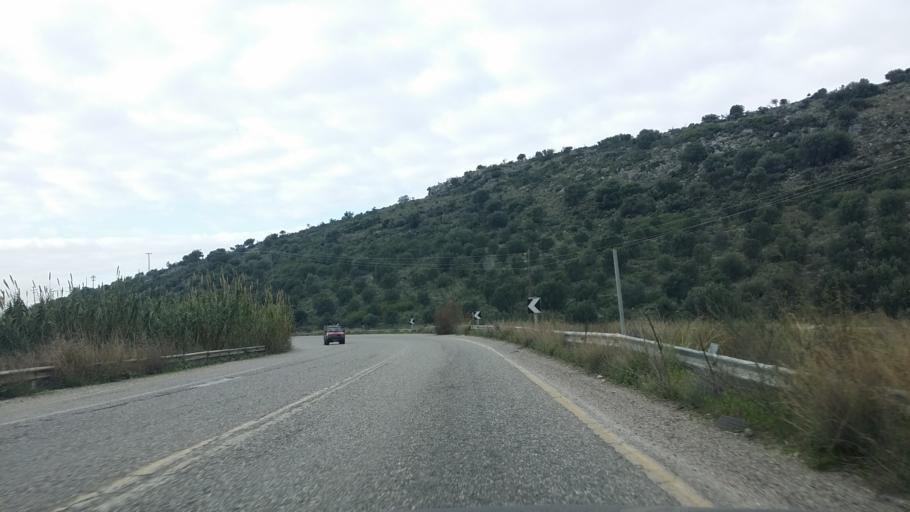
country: GR
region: West Greece
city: Aitoliko
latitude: 38.4124
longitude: 21.3962
